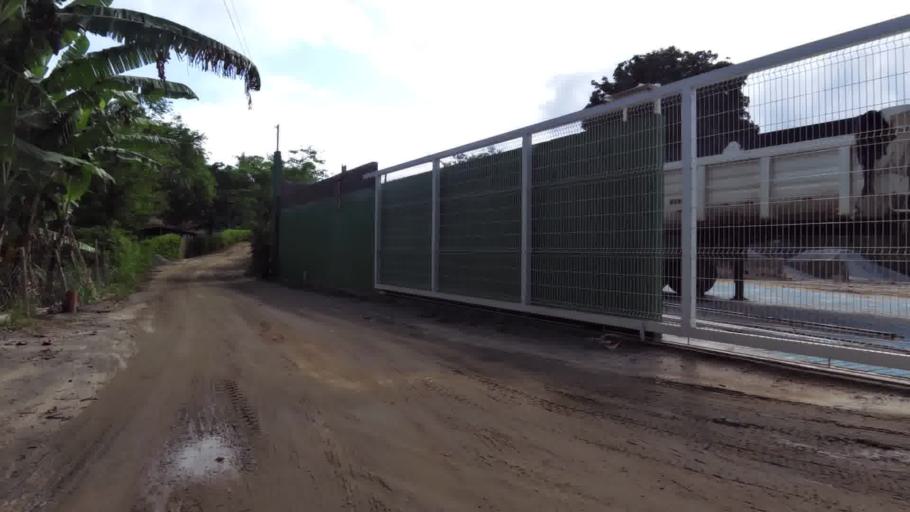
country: BR
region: Espirito Santo
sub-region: Piuma
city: Piuma
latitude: -20.8237
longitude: -40.6864
